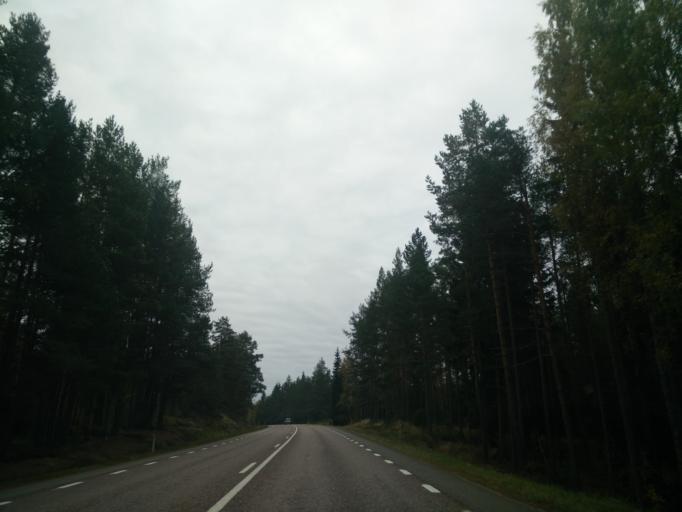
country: SE
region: Gaevleborg
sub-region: Gavle Kommun
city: Norrsundet
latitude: 60.8389
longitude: 17.2014
